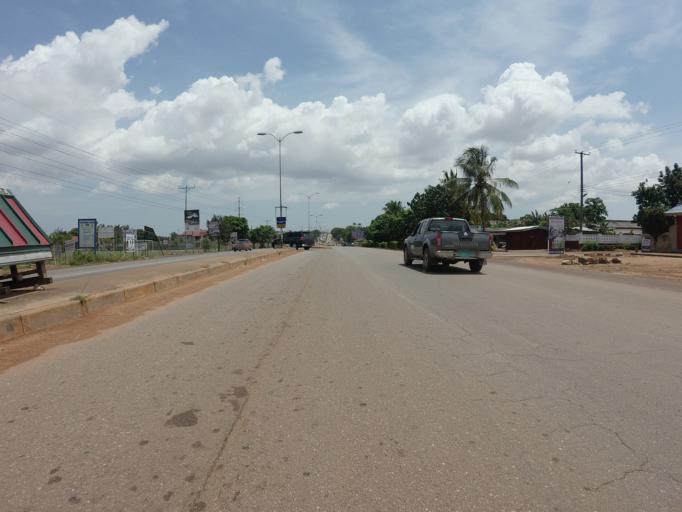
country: GH
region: Greater Accra
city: Medina Estates
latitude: 5.7408
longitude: -0.1763
